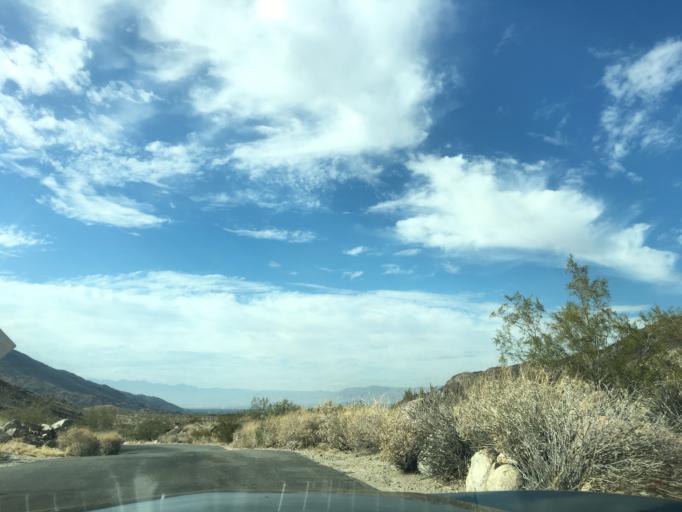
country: US
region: California
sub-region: Riverside County
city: Cathedral City
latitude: 33.7422
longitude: -116.5382
